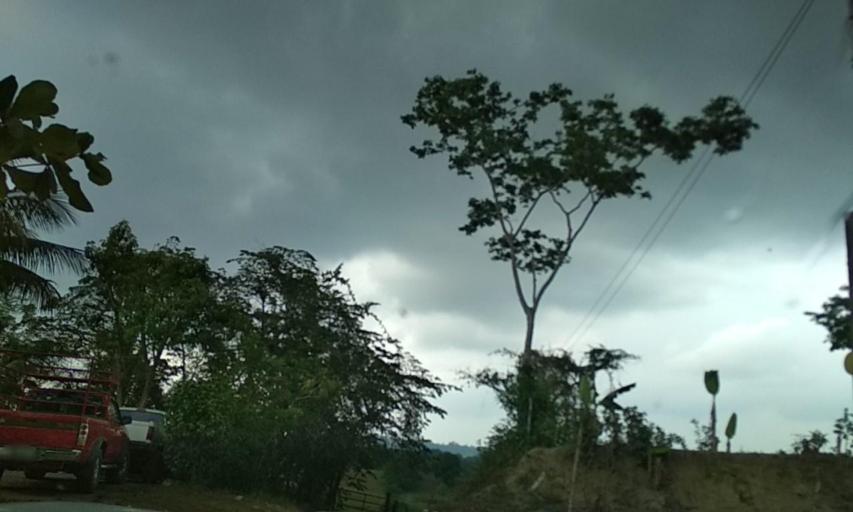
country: MX
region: Tabasco
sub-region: Huimanguillo
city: Francisco Rueda
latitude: 17.5642
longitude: -94.1125
